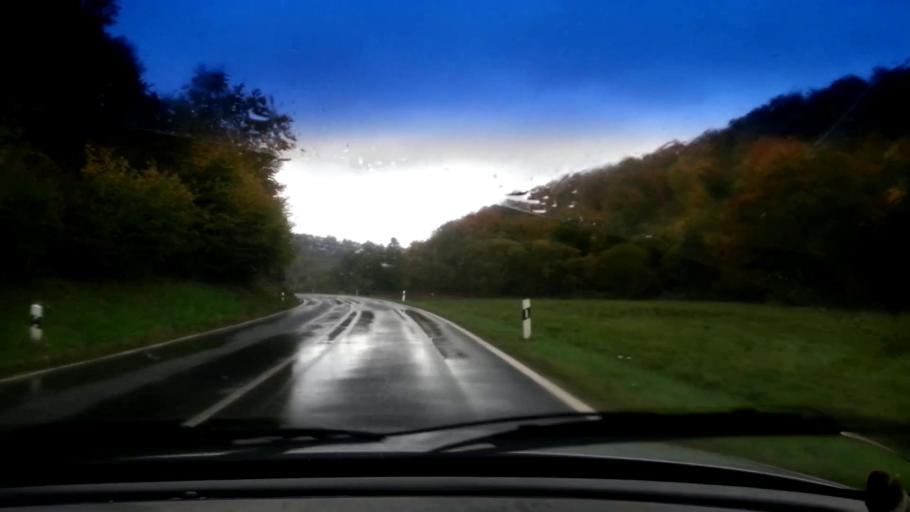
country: DE
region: Bavaria
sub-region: Upper Franconia
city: Stadelhofen
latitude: 50.0338
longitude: 11.2034
